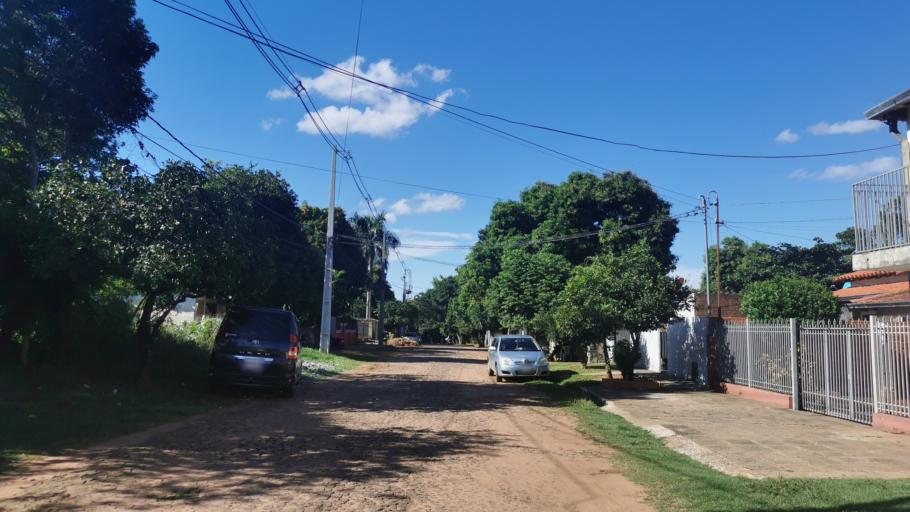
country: PY
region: Central
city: San Lorenzo
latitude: -25.3281
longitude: -57.5082
